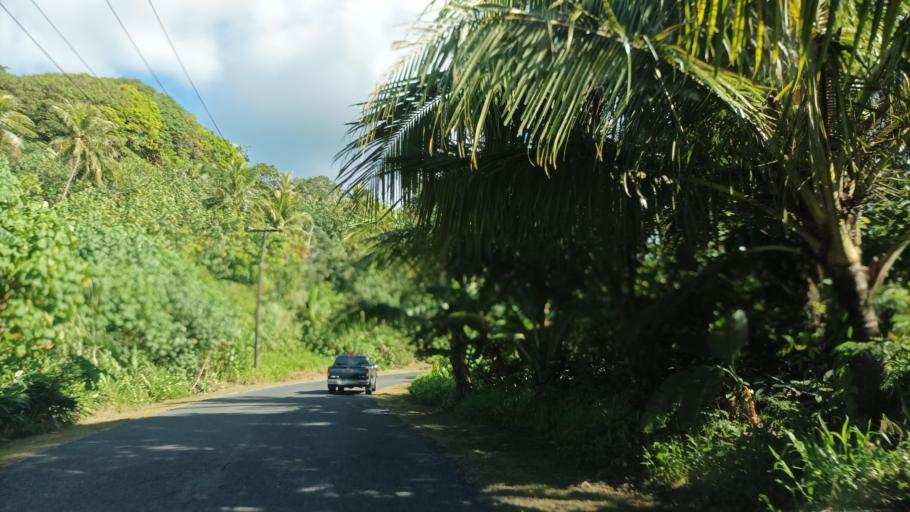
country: FM
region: Pohnpei
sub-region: Kolonia Municipality
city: Kolonia
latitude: 6.9634
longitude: 158.2499
